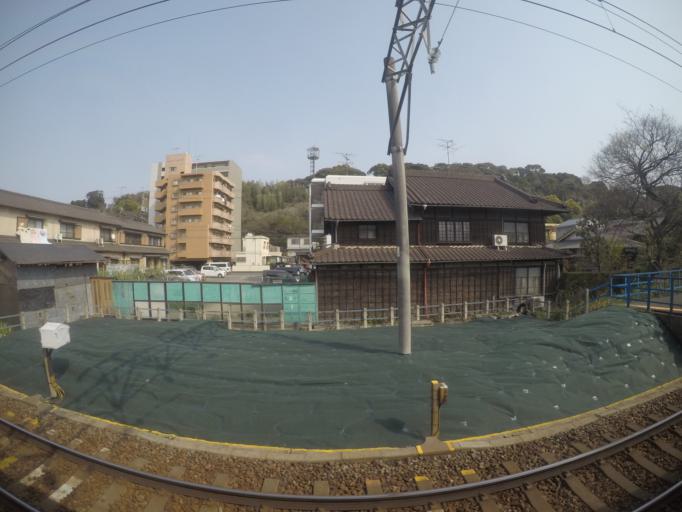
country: JP
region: Aichi
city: Obu
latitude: 35.0357
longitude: 136.8999
